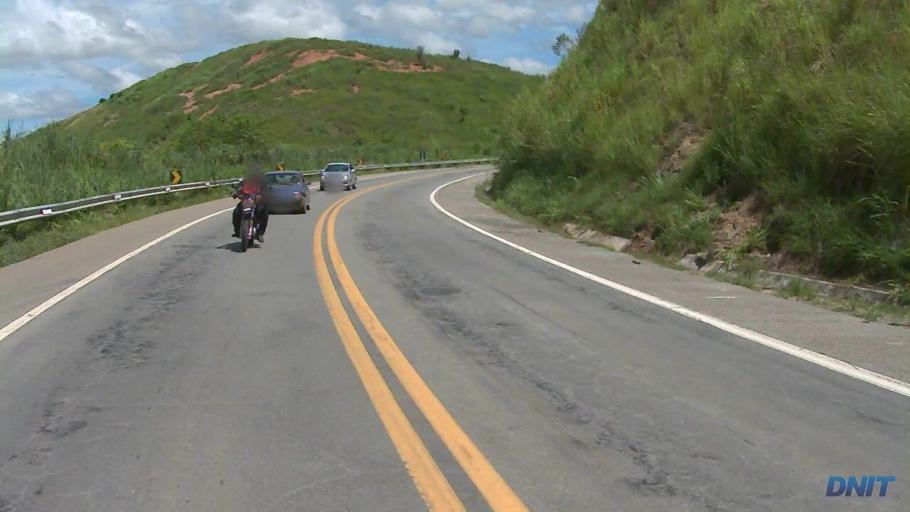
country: BR
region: Minas Gerais
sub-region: Governador Valadares
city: Governador Valadares
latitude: -18.9657
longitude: -42.0863
